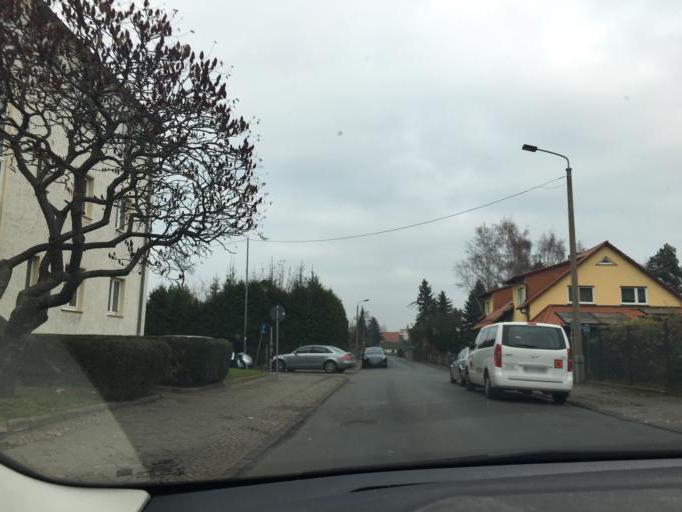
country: DE
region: Saxony
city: Taucha
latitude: 51.3462
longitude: 12.4588
